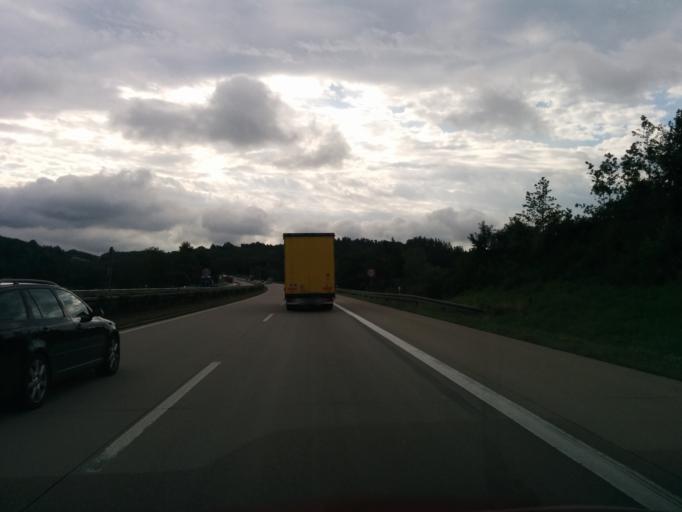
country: DE
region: Bavaria
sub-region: Lower Bavaria
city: Bogen
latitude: 48.9354
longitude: 12.6717
